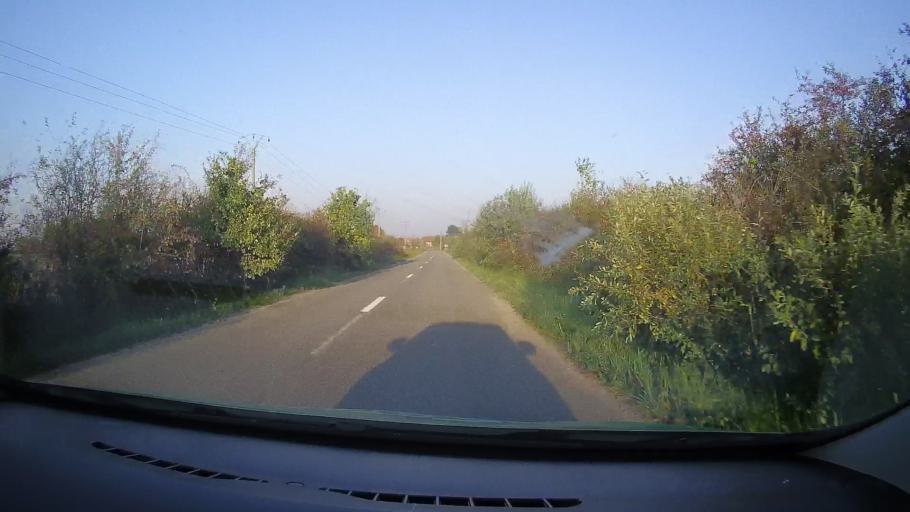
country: RO
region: Arad
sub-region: Comuna Barsa
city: Barsa
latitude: 46.3566
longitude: 22.0243
